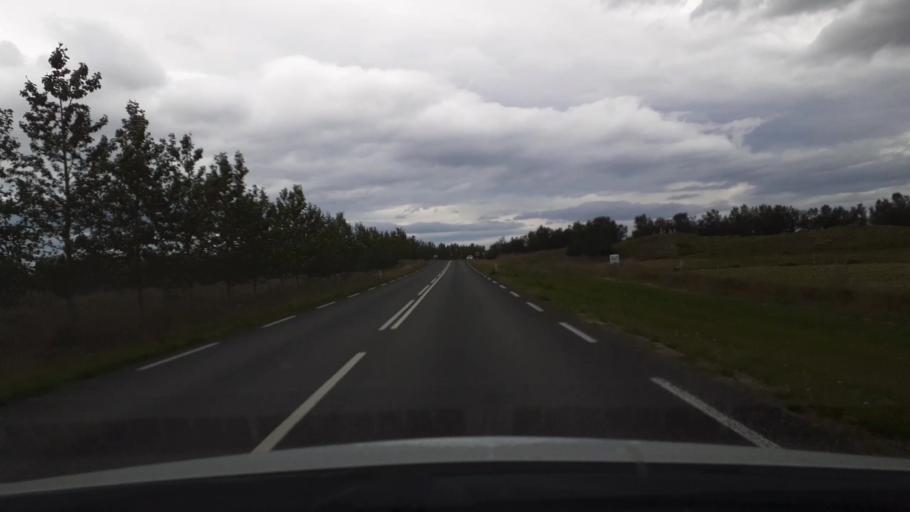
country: IS
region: West
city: Borgarnes
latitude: 64.5601
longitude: -21.7547
